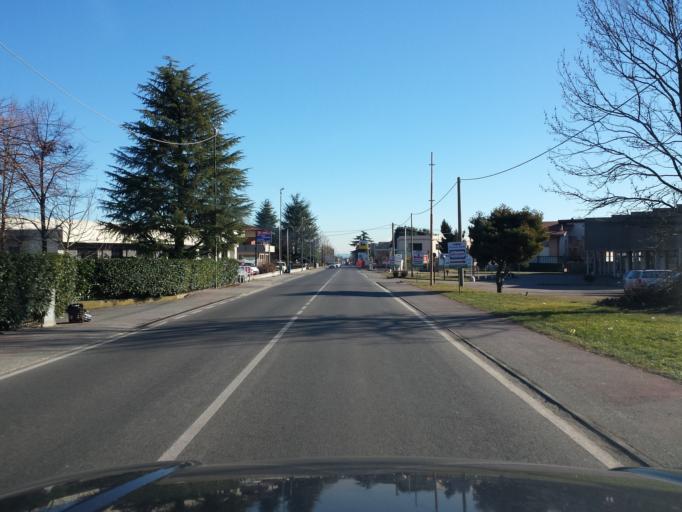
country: IT
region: Piedmont
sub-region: Provincia di Torino
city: Feletto
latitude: 45.3166
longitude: 7.7342
